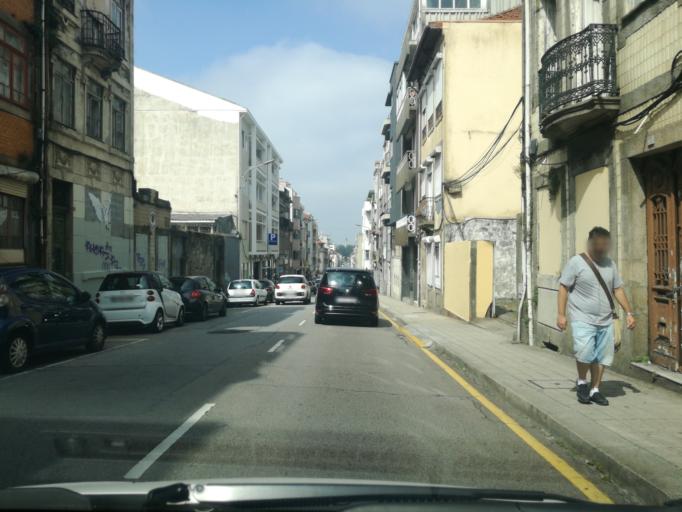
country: PT
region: Porto
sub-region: Porto
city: Porto
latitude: 41.1559
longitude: -8.6160
